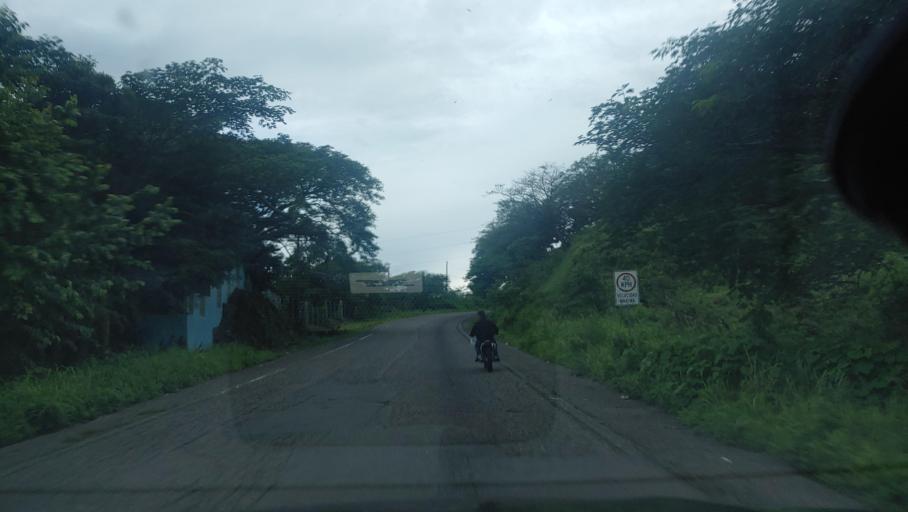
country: HN
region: Choluteca
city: Corpus
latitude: 13.3646
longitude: -86.9921
